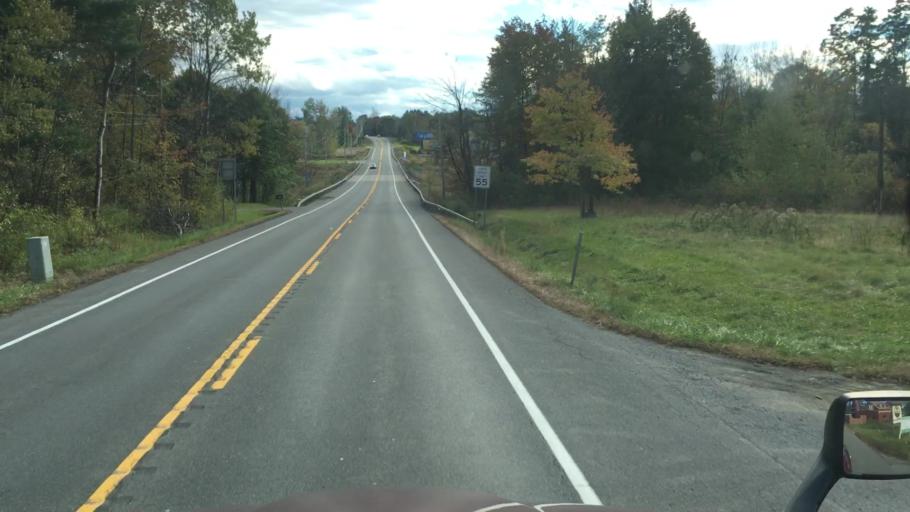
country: US
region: New York
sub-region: Saratoga County
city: Ballston Spa
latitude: 42.9741
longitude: -73.8623
